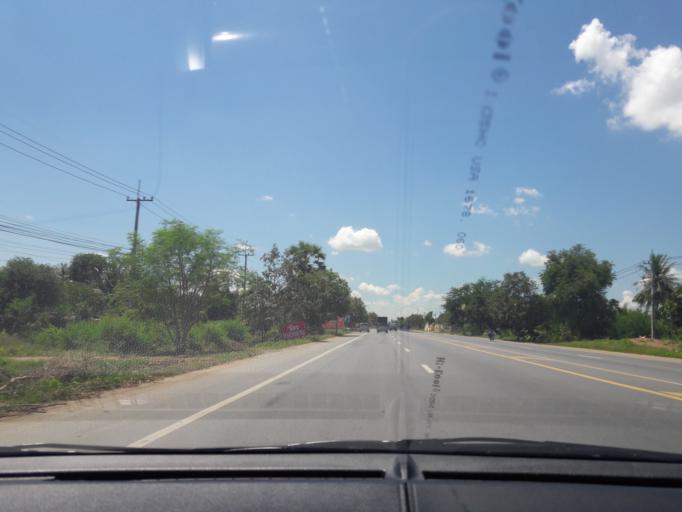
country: TH
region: Kanchanaburi
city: Tha Maka
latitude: 14.0332
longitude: 99.8241
